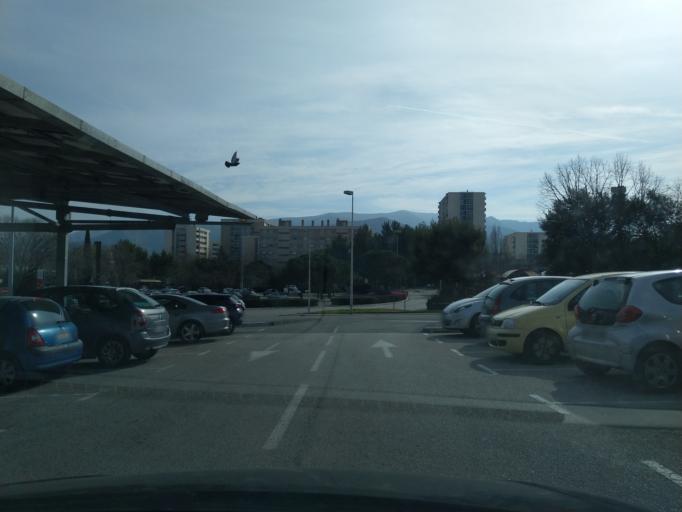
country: FR
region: Provence-Alpes-Cote d'Azur
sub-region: Departement des Bouches-du-Rhone
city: Marseille 12
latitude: 43.2956
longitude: 5.4418
